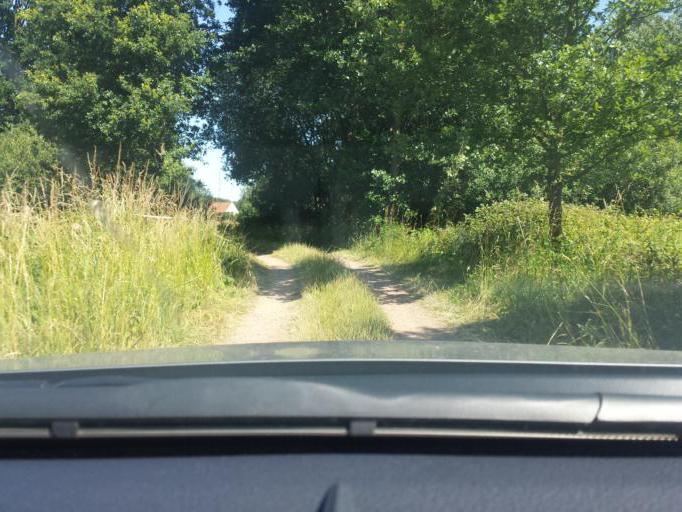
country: BE
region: Flanders
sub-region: Provincie Limburg
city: Lummen
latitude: 50.9714
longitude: 5.1783
